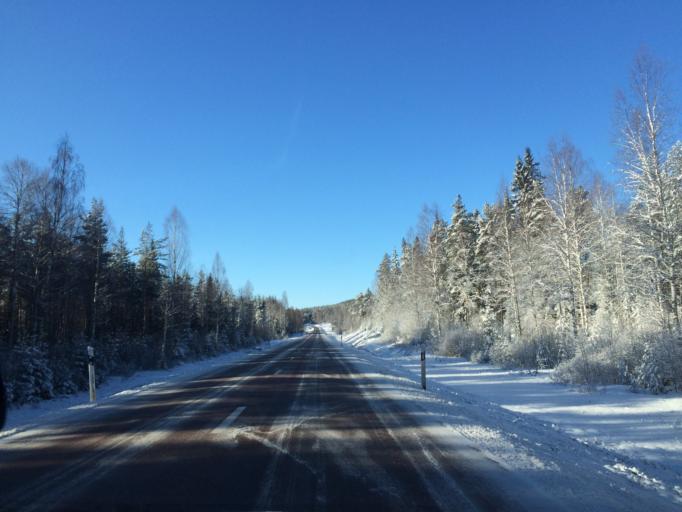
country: SE
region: Dalarna
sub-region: Mora Kommun
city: Mora
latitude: 60.8973
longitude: 14.3842
